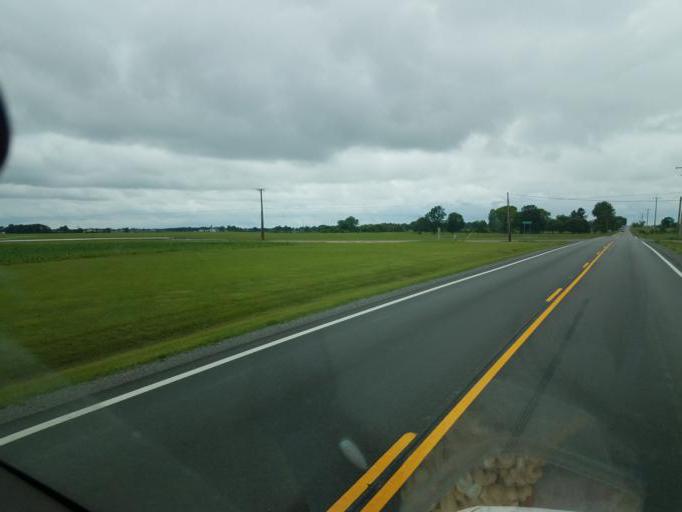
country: US
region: Ohio
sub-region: Marion County
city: Marion
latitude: 40.5633
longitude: -83.0460
